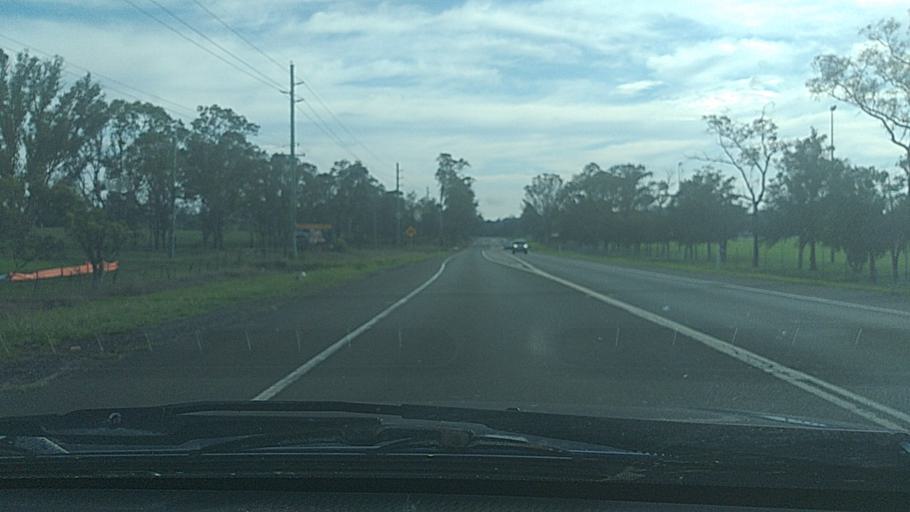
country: AU
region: New South Wales
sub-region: Penrith Municipality
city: Glenmore Park
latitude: -33.8134
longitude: 150.6910
